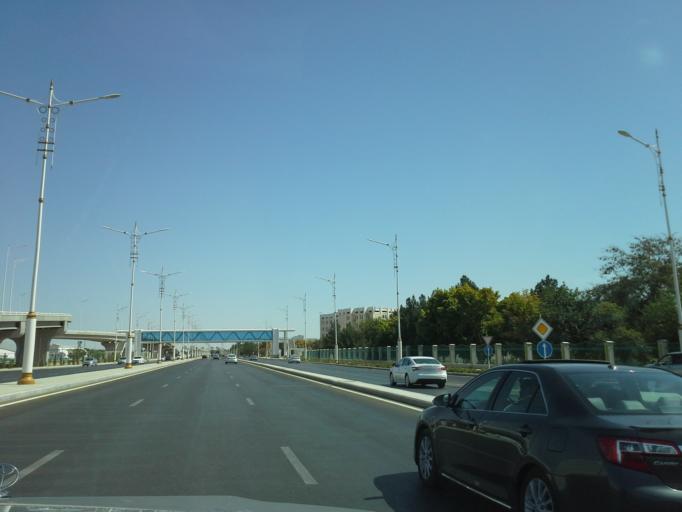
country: TM
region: Ahal
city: Ashgabat
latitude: 37.9263
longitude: 58.4301
